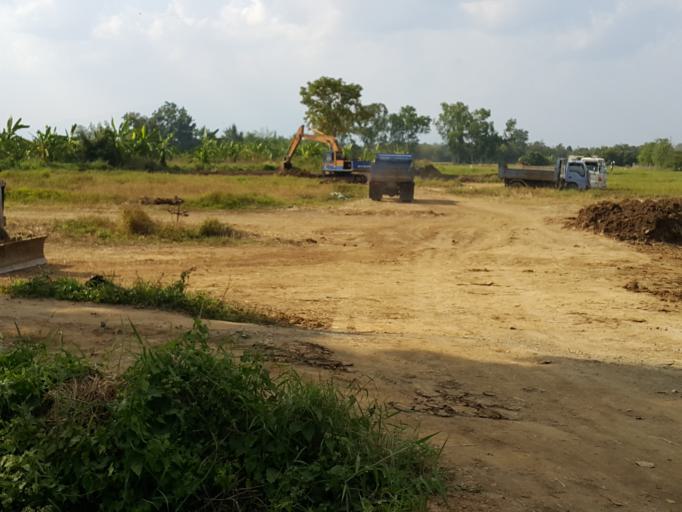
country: TH
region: Chiang Mai
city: San Kamphaeng
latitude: 18.7812
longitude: 99.1100
